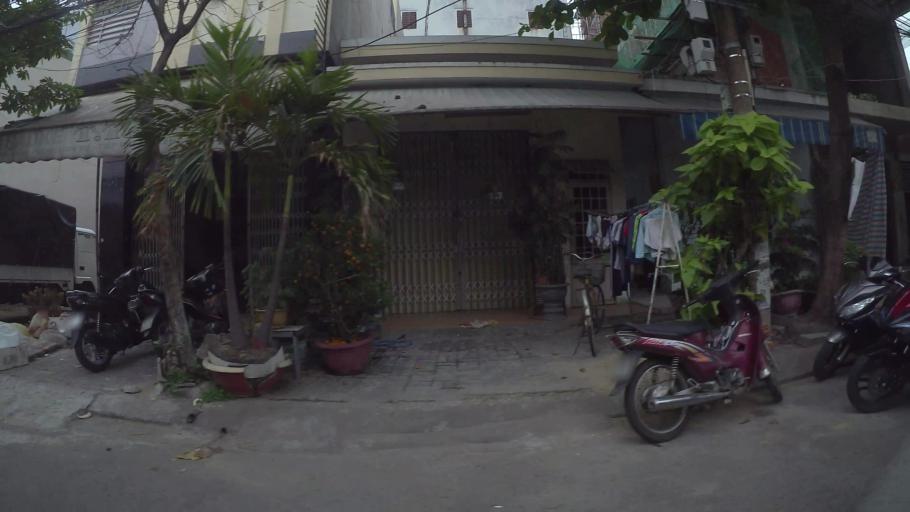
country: VN
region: Da Nang
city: Thanh Khe
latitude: 16.0615
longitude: 108.1811
